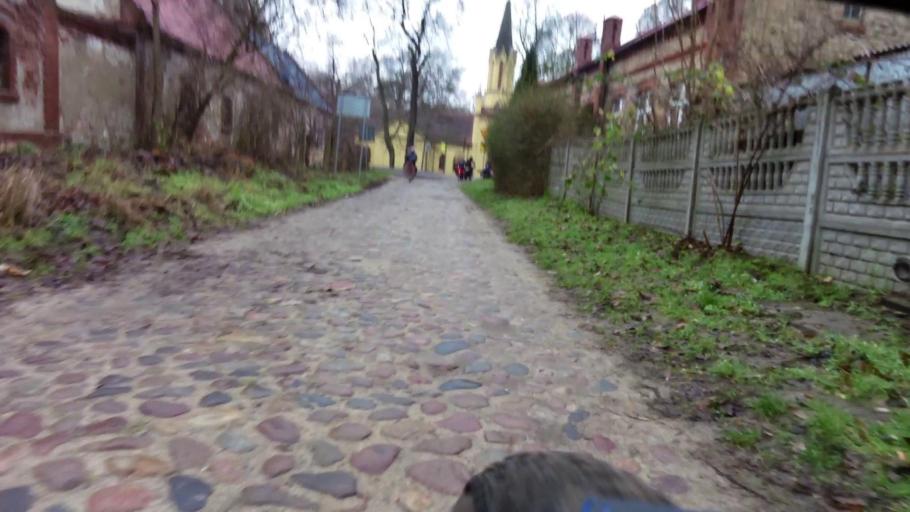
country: PL
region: Lubusz
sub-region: Powiat gorzowski
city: Kostrzyn nad Odra
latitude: 52.6208
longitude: 14.7049
